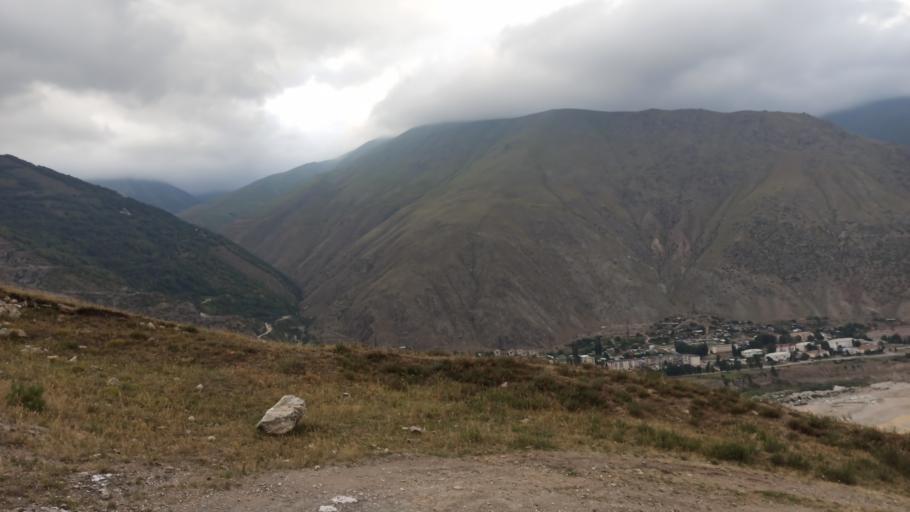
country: RU
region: Kabardino-Balkariya
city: Tyrnyauz
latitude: 43.3922
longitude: 42.9266
